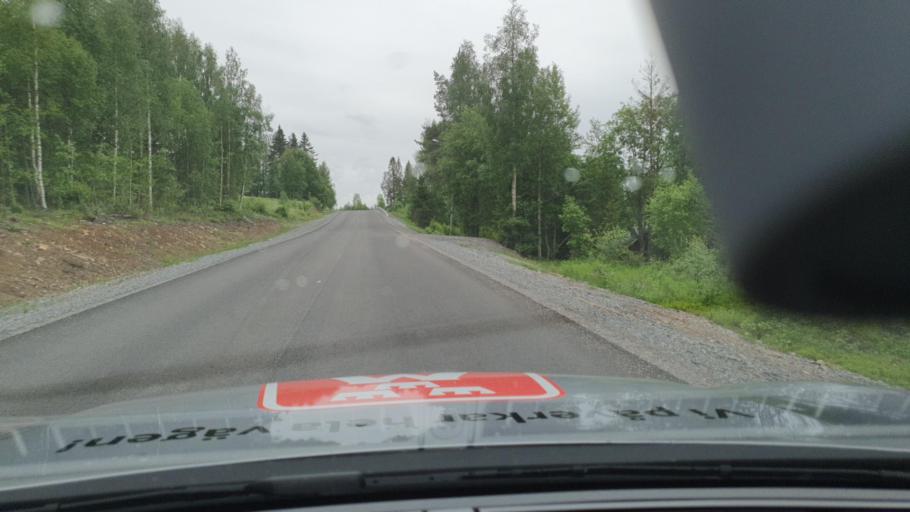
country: SE
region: Norrbotten
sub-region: Overtornea Kommun
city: OEvertornea
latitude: 66.5957
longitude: 23.3090
